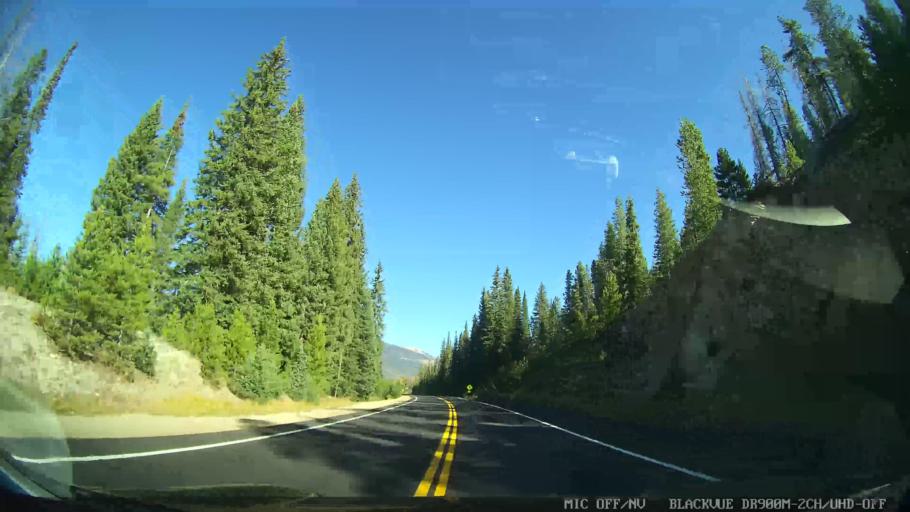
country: US
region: Colorado
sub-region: Grand County
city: Granby
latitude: 40.3230
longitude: -105.8526
